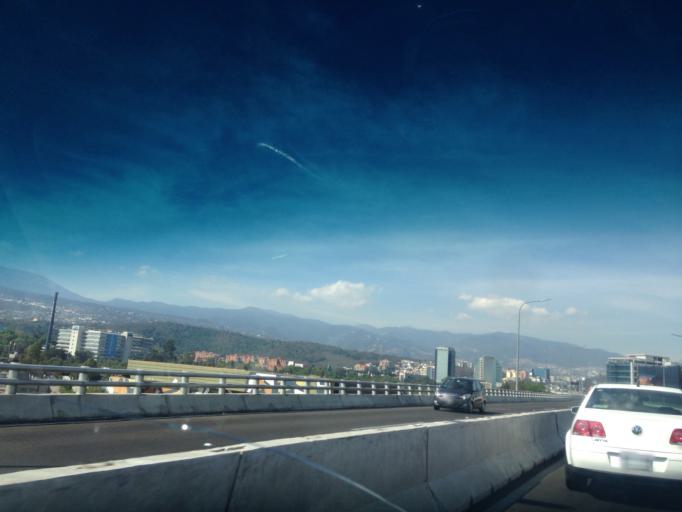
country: MX
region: Mexico City
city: Tlalpan
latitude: 19.3034
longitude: -99.1773
